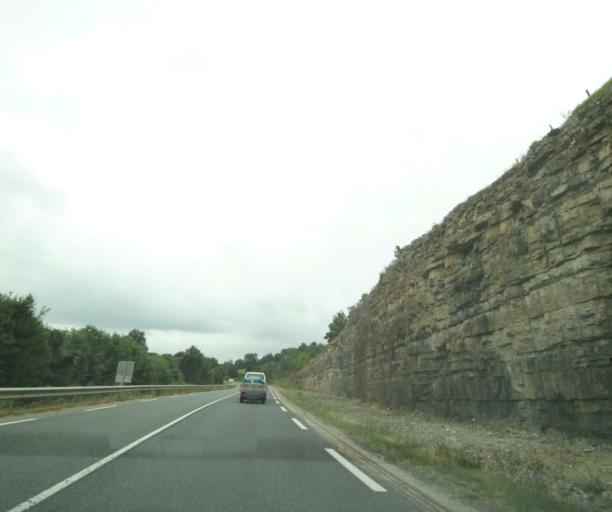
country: FR
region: Midi-Pyrenees
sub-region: Departement de l'Aveyron
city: Laissac
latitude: 44.3537
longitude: 2.9203
